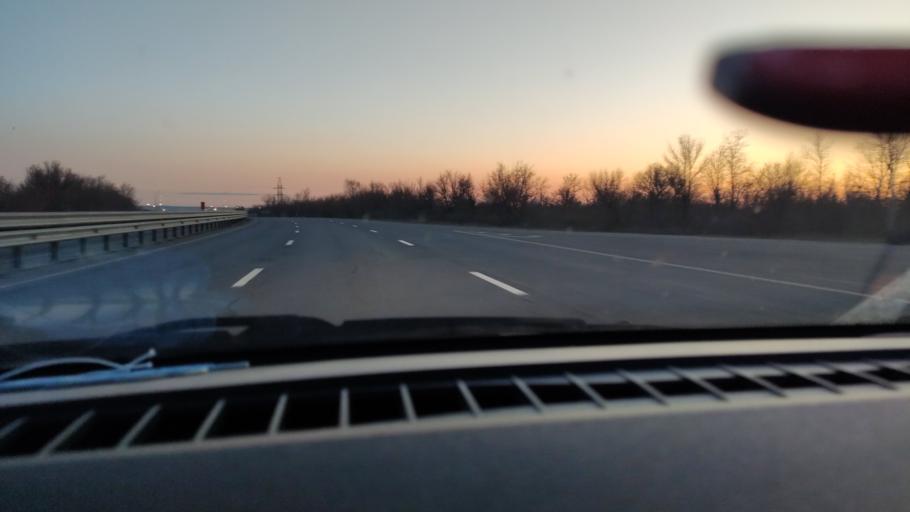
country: RU
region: Saratov
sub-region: Saratovskiy Rayon
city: Saratov
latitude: 51.6542
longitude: 45.9977
